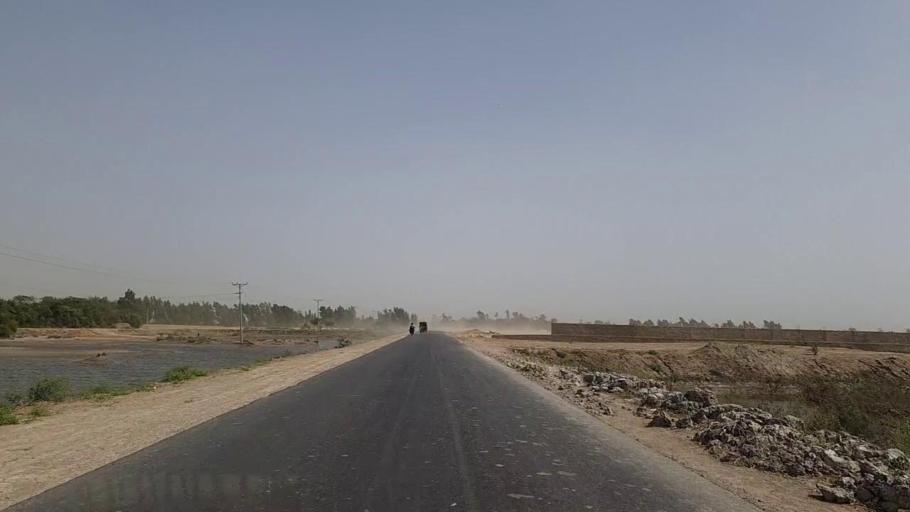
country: PK
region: Sindh
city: Tando Bago
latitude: 24.7958
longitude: 68.9499
